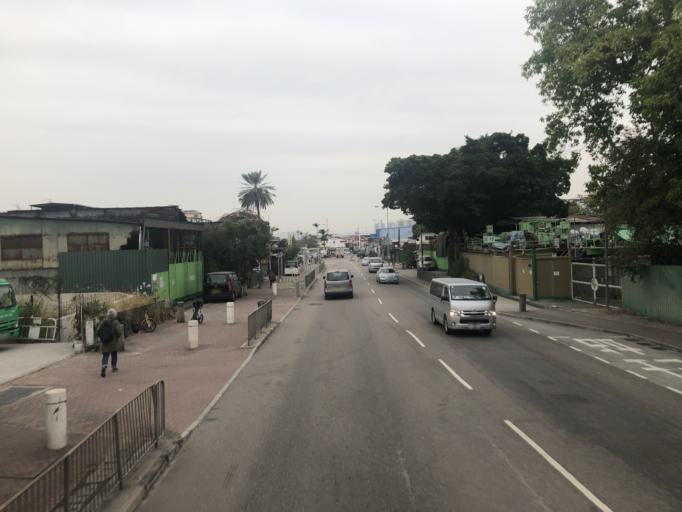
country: HK
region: Yuen Long
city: Yuen Long Kau Hui
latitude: 22.4333
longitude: 113.9926
